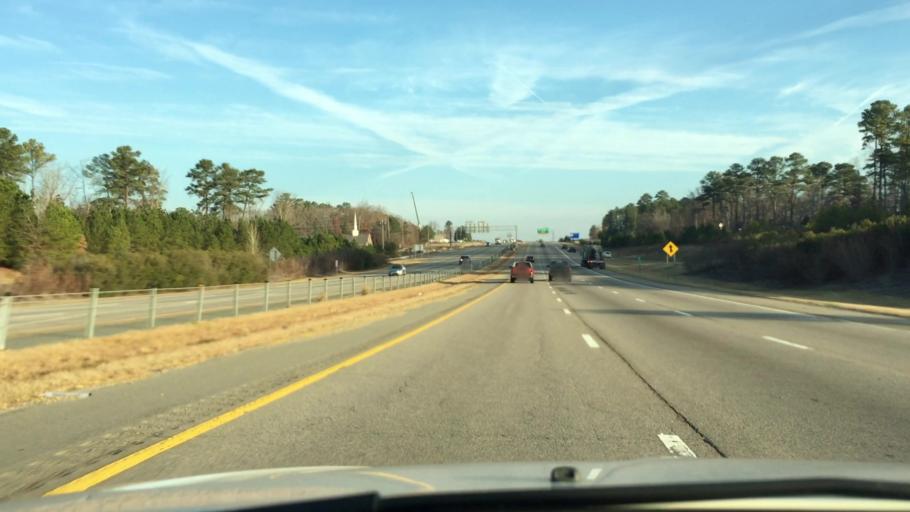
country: US
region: North Carolina
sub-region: Lee County
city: Sanford
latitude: 35.5127
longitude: -79.1874
